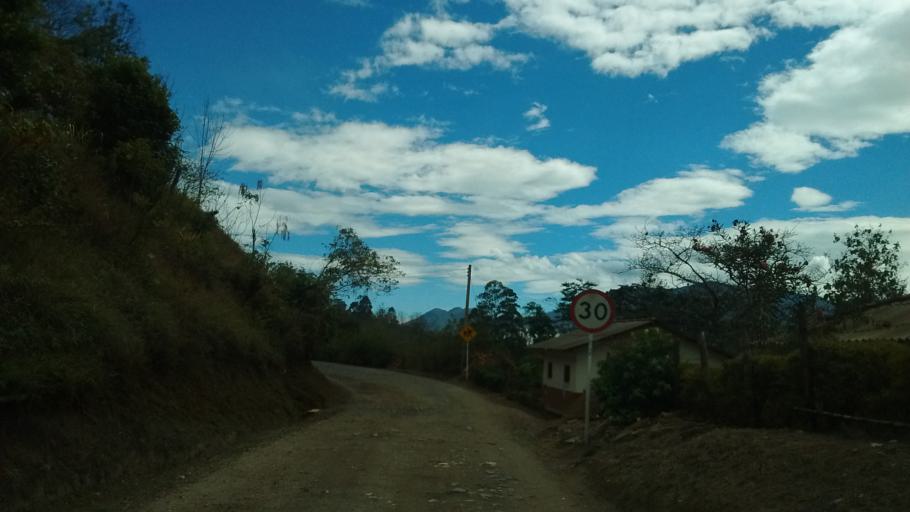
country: CO
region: Cauca
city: Almaguer
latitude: 1.8454
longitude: -76.9221
